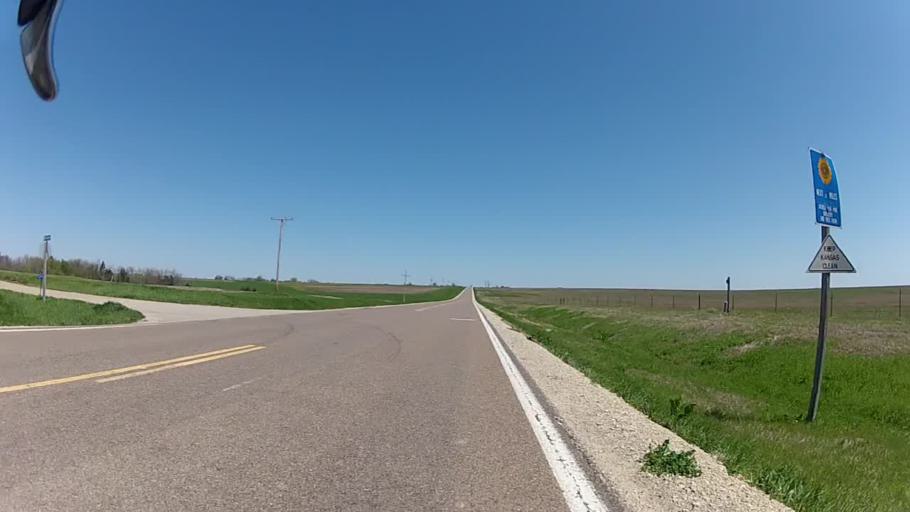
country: US
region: Kansas
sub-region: Wabaunsee County
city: Alma
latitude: 38.9421
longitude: -96.5201
